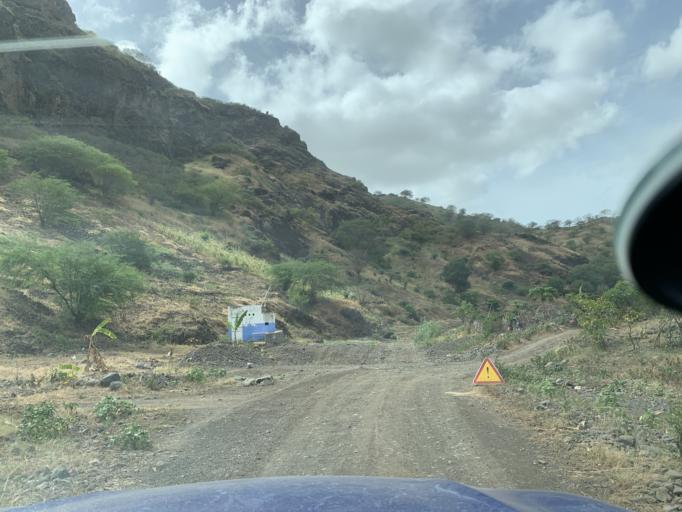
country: CV
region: Santa Cruz
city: Santa Cruz
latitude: 15.1084
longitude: -23.5731
